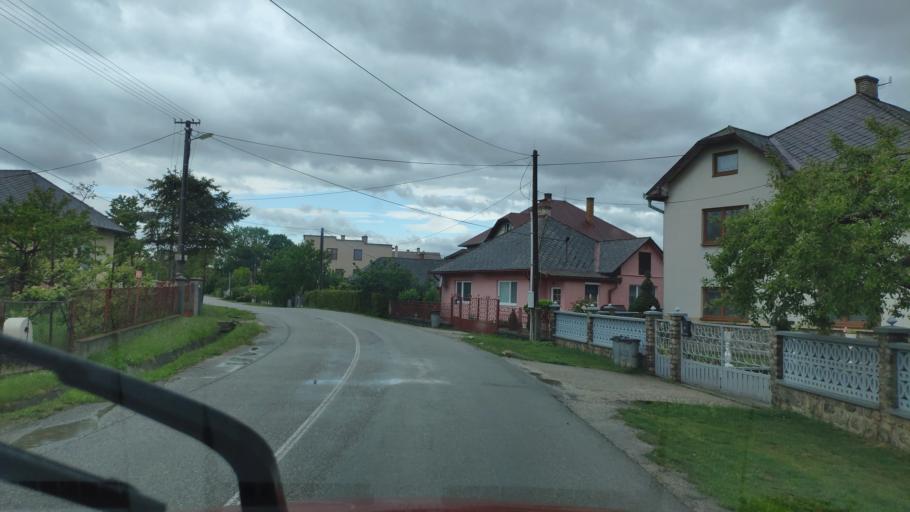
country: SK
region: Kosicky
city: Moldava nad Bodvou
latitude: 48.5433
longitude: 21.0466
